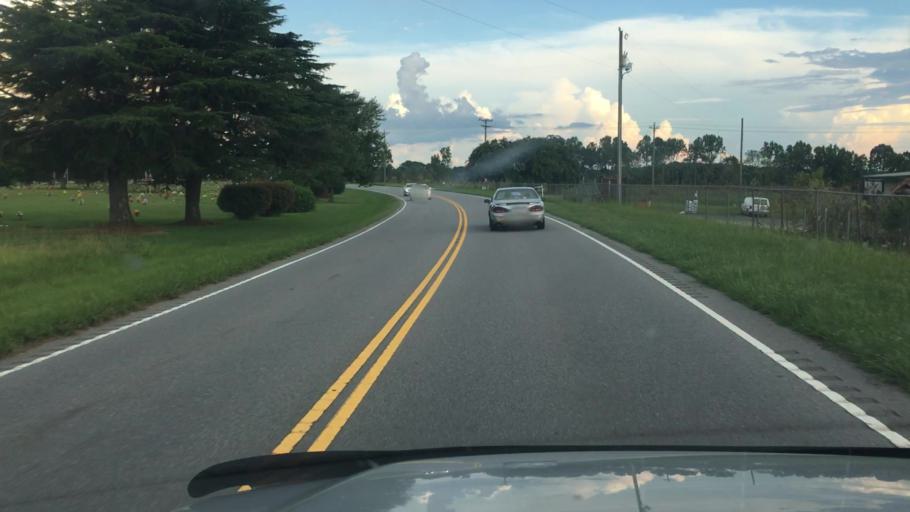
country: US
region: South Carolina
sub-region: Cherokee County
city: Gaffney
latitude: 35.1066
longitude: -81.6971
